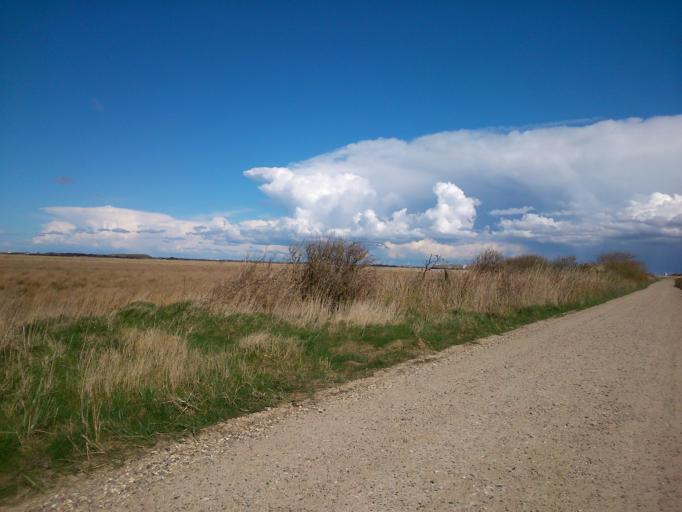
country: DK
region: Central Jutland
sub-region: Ringkobing-Skjern Kommune
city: Hvide Sande
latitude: 56.0992
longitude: 8.1338
